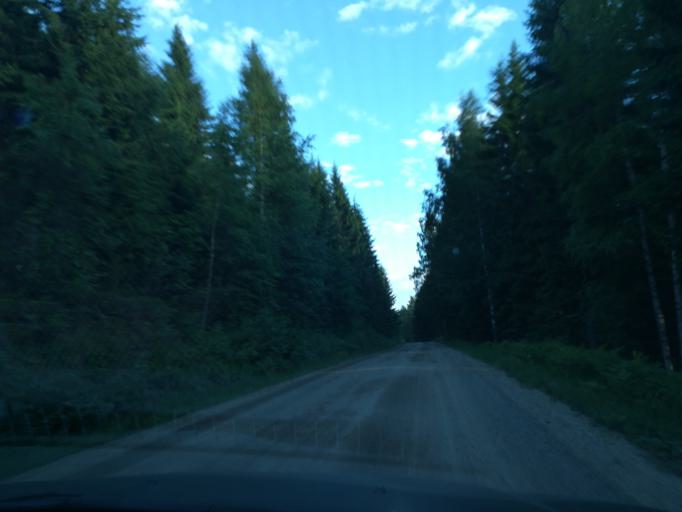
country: FI
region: Southern Savonia
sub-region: Mikkeli
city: Puumala
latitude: 61.6102
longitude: 28.1154
